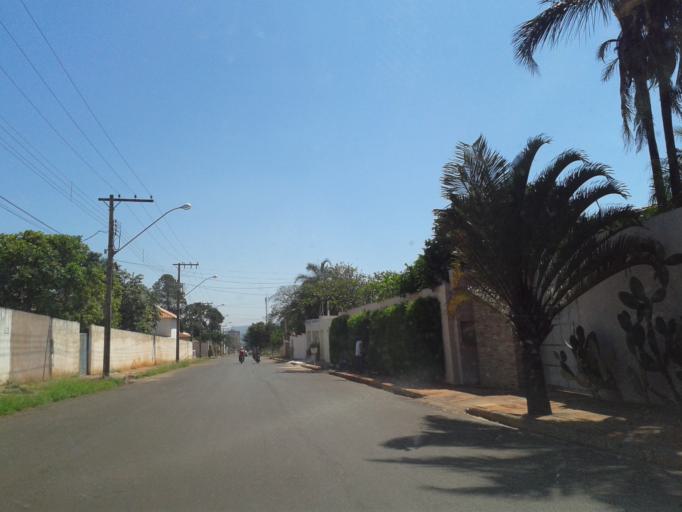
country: BR
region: Minas Gerais
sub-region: Ituiutaba
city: Ituiutaba
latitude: -18.9910
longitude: -49.4569
